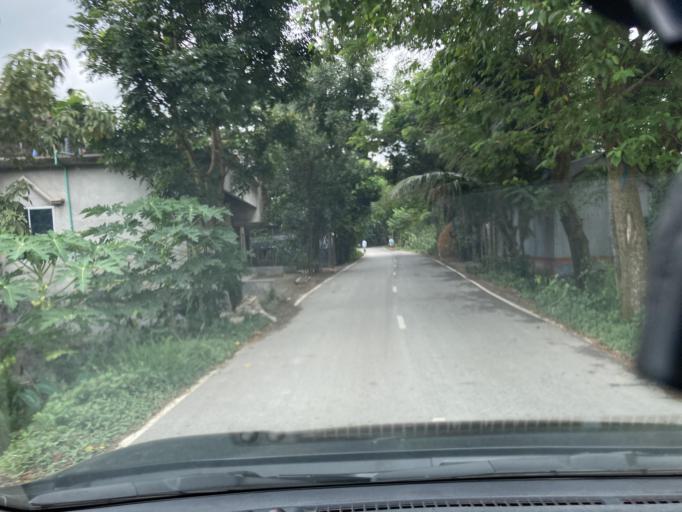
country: BD
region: Dhaka
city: Azimpur
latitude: 23.7823
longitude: 90.2120
